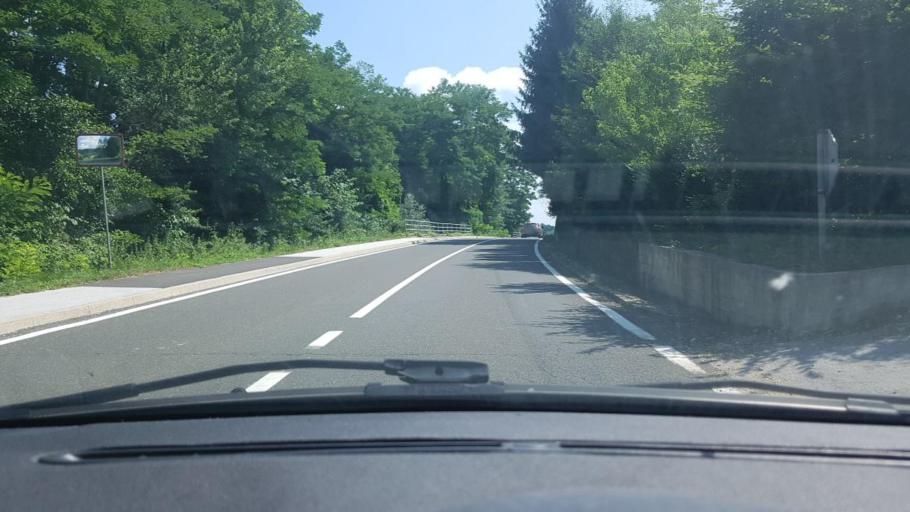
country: HR
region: Krapinsko-Zagorska
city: Pregrada
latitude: 46.2070
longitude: 15.7577
